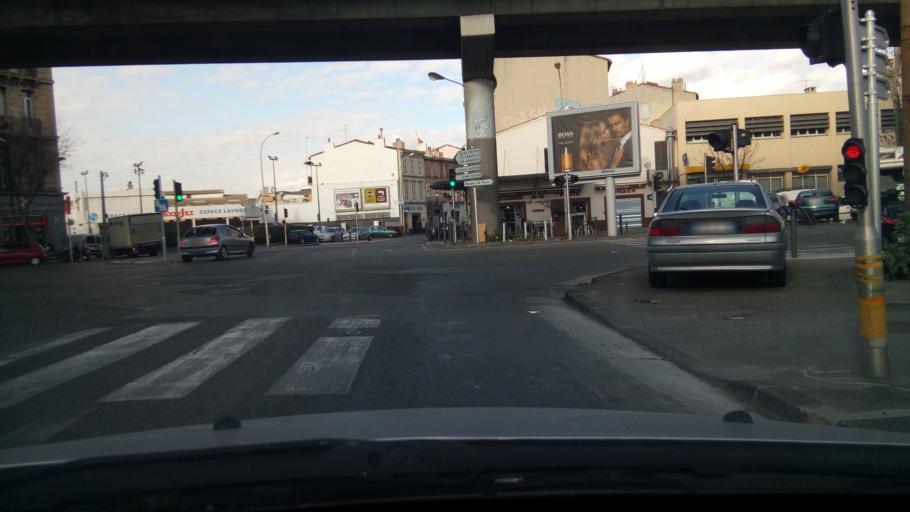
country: FR
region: Provence-Alpes-Cote d'Azur
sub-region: Departement des Bouches-du-Rhone
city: Marseille 03
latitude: 43.3187
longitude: 5.3679
